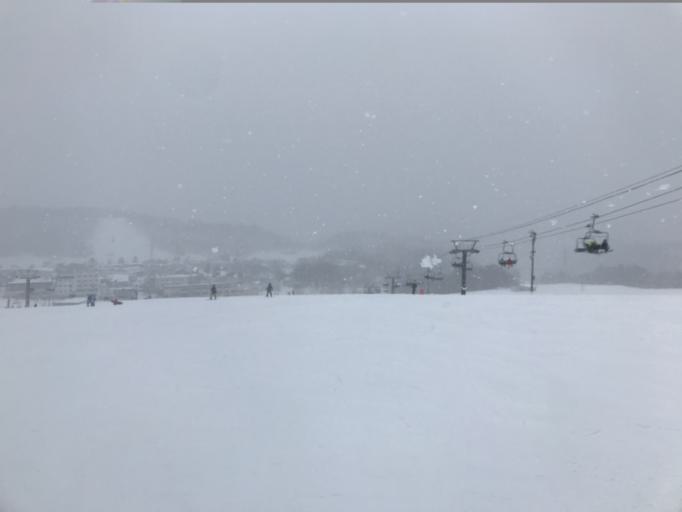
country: JP
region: Nagano
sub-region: Kitaazumi Gun
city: Hakuba
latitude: 36.7478
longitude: 137.8649
